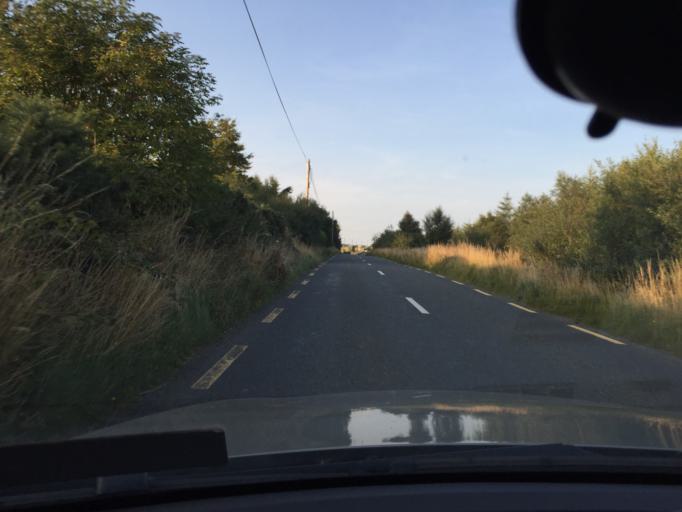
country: IE
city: Newtownmountkennedy
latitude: 53.0567
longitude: -6.2359
